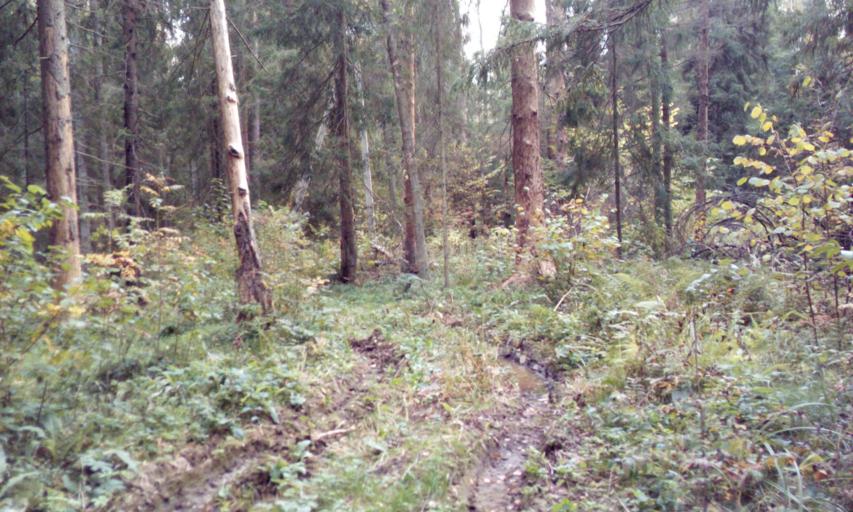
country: RU
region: Moskovskaya
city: Selyatino
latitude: 55.4859
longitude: 36.9633
